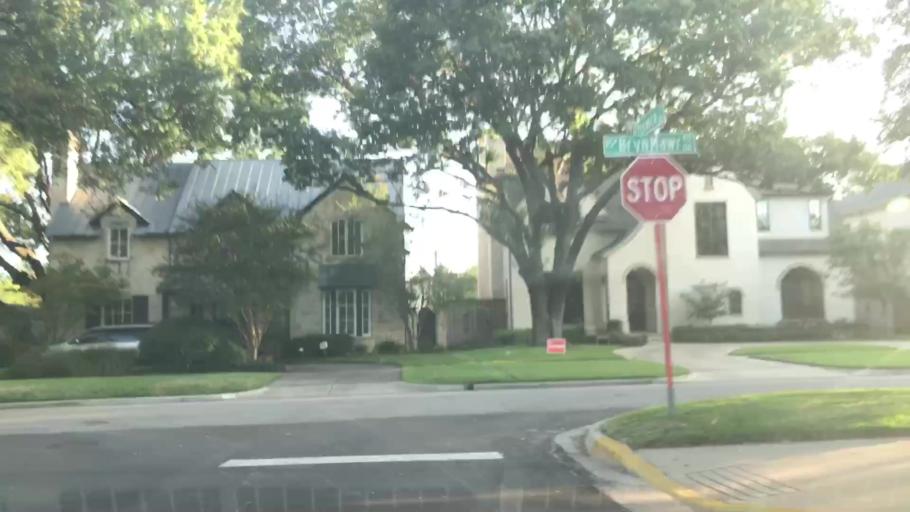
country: US
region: Texas
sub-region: Dallas County
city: University Park
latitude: 32.8560
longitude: -96.8019
